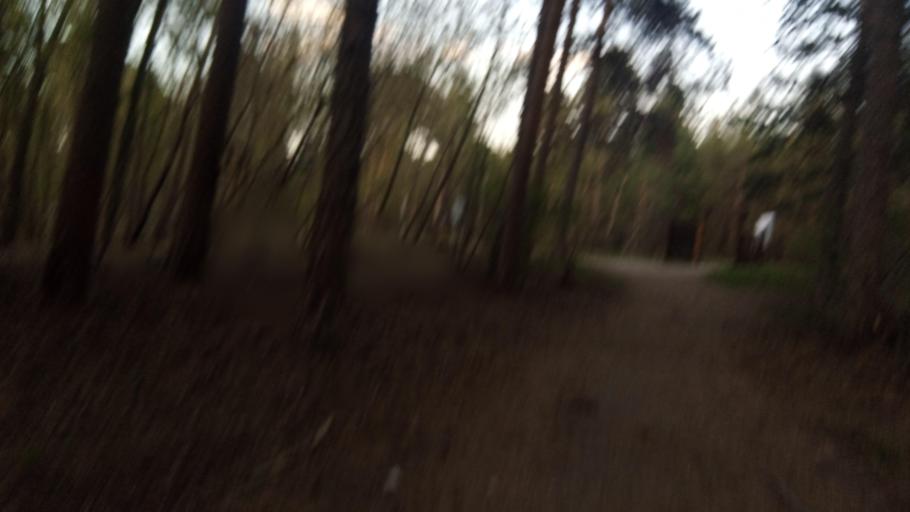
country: RU
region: Chelyabinsk
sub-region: Gorod Chelyabinsk
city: Chelyabinsk
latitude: 55.1664
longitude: 61.3399
